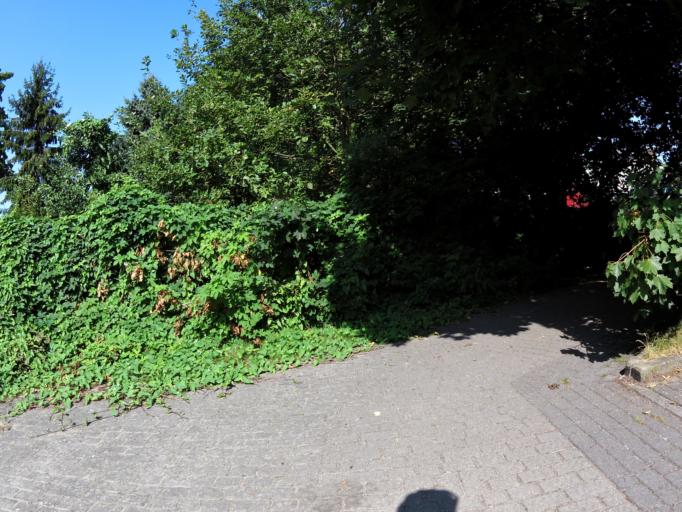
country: DE
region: Mecklenburg-Vorpommern
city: Seebad Heringsdorf
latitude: 53.9414
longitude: 14.1803
